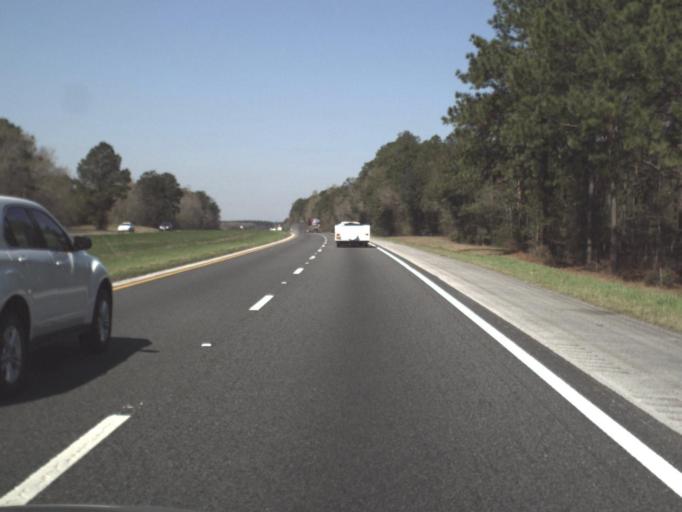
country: US
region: Florida
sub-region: Jackson County
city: Sneads
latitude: 30.6795
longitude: -85.0859
